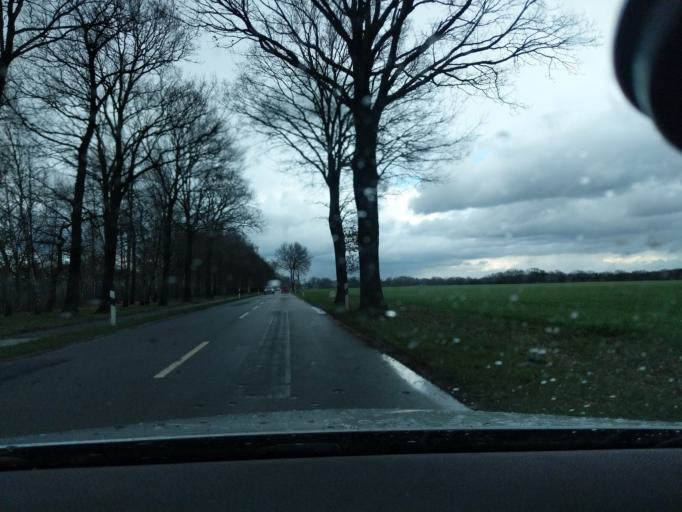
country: DE
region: Lower Saxony
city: Kutenholz
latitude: 53.5108
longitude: 9.3657
